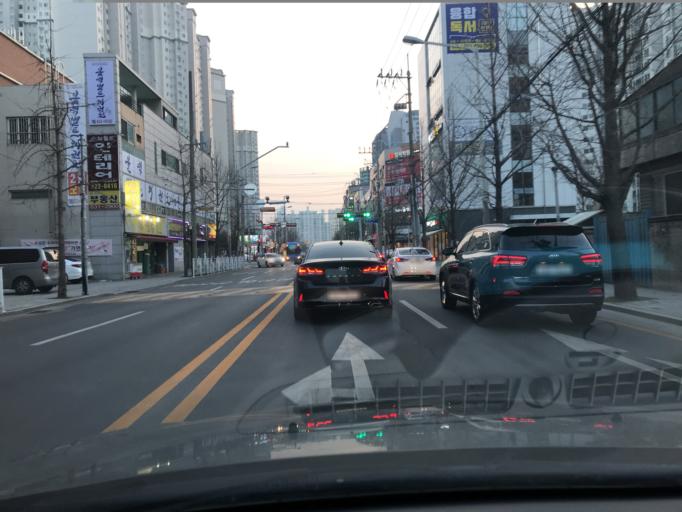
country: KR
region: Daegu
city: Hwawon
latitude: 35.8174
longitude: 128.5184
